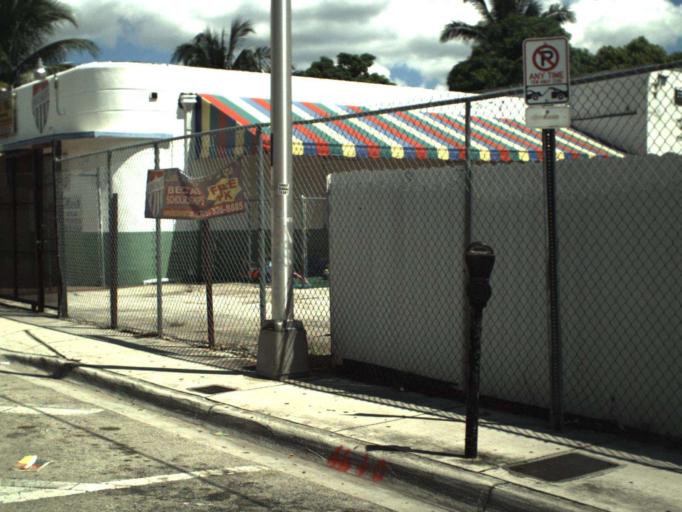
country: US
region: Florida
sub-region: Miami-Dade County
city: Miami
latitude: 25.7759
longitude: -80.2078
